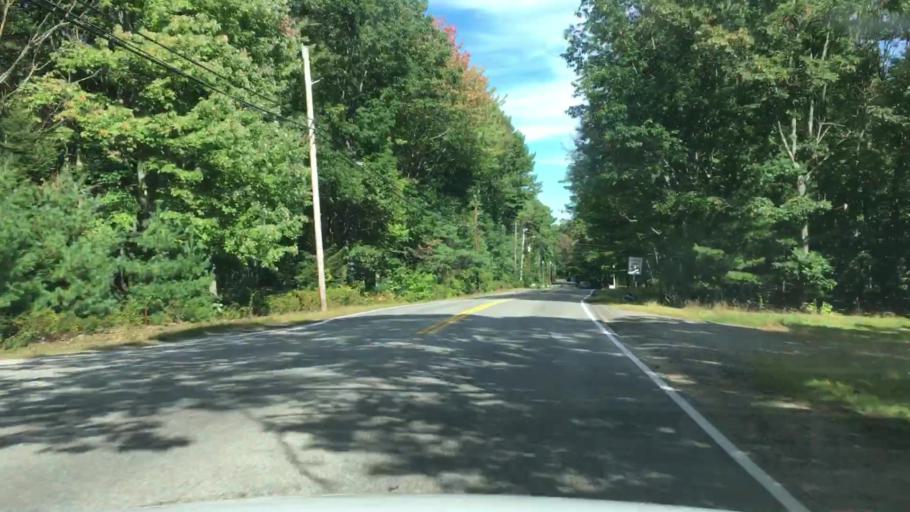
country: US
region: Maine
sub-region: Cumberland County
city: West Scarborough
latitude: 43.6032
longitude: -70.4215
